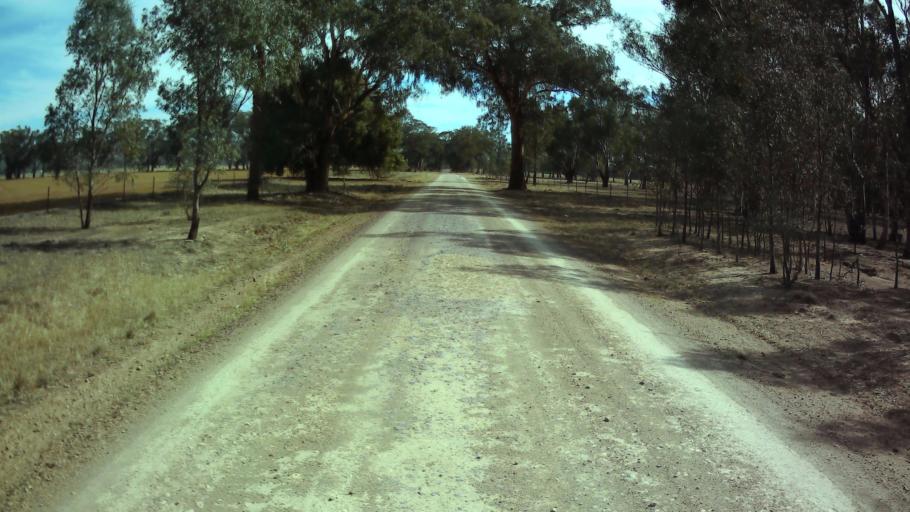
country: AU
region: New South Wales
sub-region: Weddin
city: Grenfell
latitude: -33.7023
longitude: 148.3019
